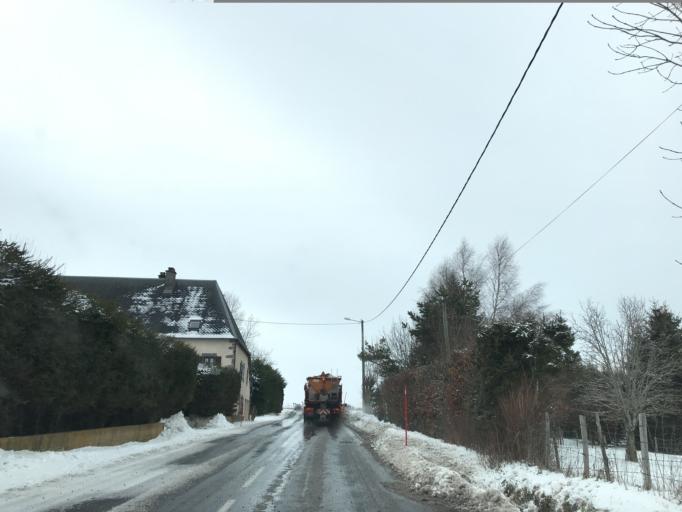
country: FR
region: Auvergne
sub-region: Departement du Puy-de-Dome
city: Aydat
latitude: 45.6551
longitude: 2.9123
